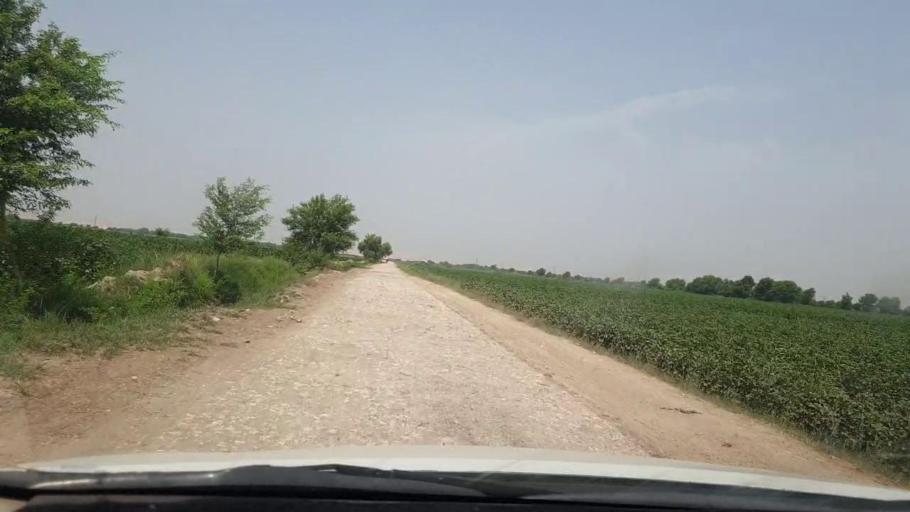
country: PK
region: Sindh
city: Rohri
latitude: 27.4984
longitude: 69.0148
